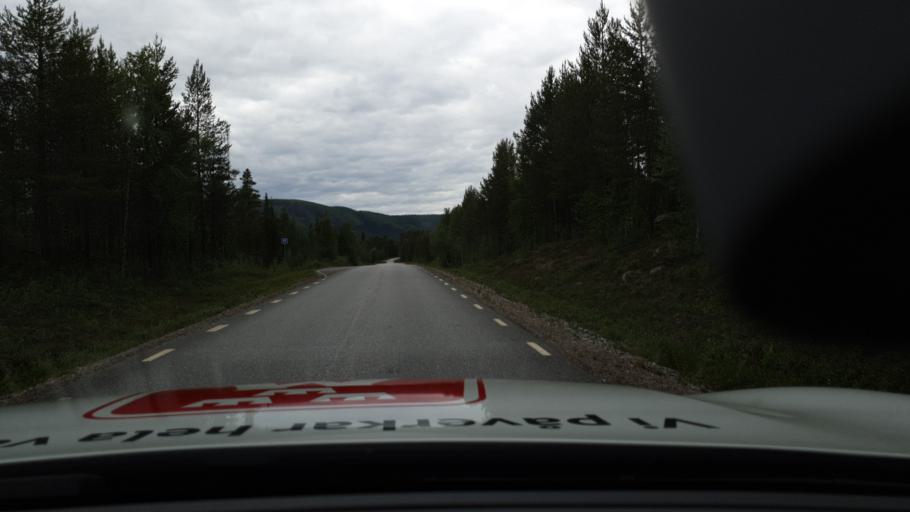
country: SE
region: Norrbotten
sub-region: Arjeplogs Kommun
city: Arjeplog
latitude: 66.8794
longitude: 18.2367
